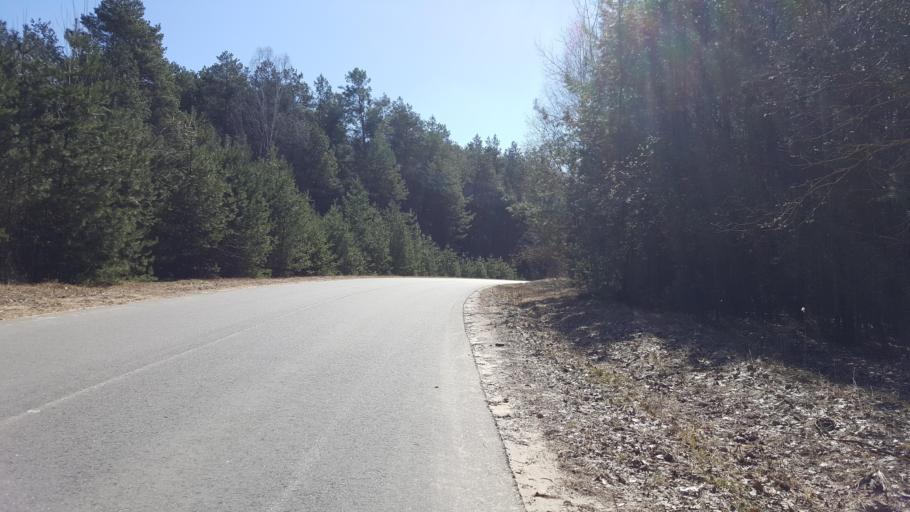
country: BY
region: Brest
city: Kamyanyets
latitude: 52.3585
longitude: 23.8200
